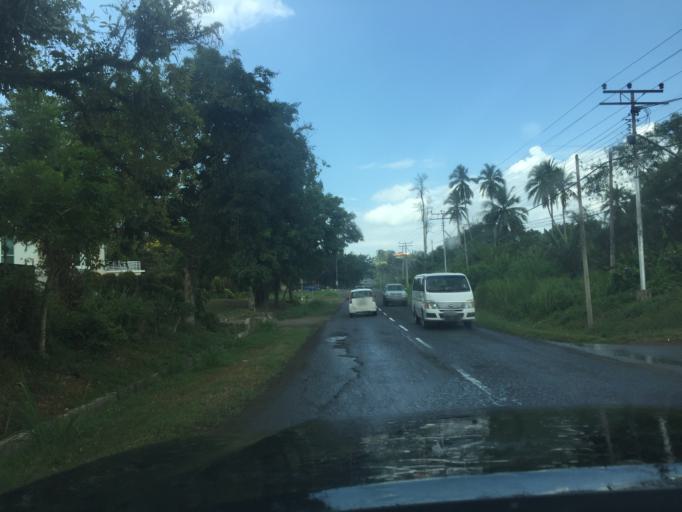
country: MY
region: Sabah
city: Lahad Datu
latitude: 5.0438
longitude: 118.3391
